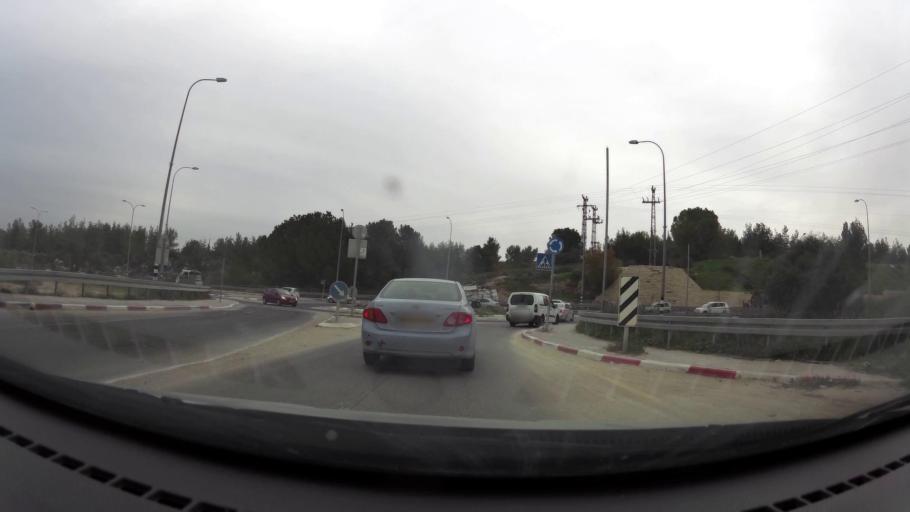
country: IL
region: Jerusalem
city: Bet Shemesh
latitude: 31.7030
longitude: 35.0086
